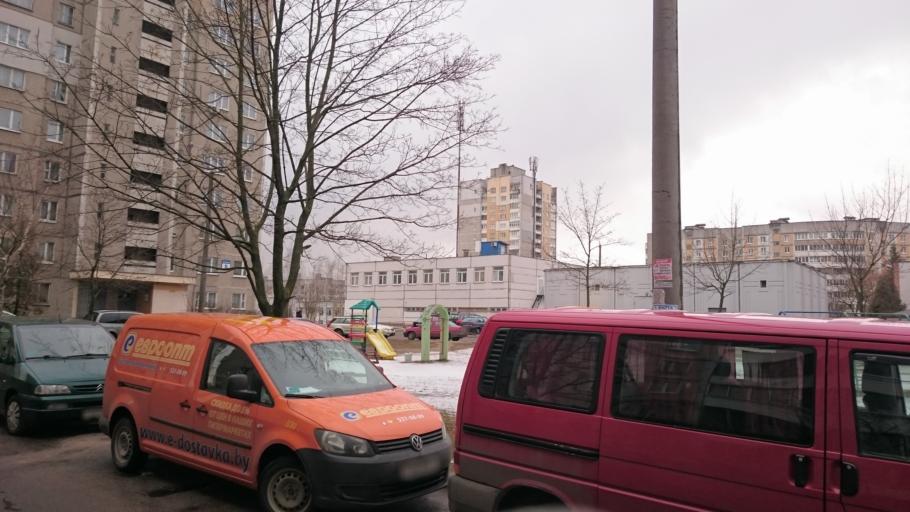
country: BY
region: Minsk
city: Borovlyany
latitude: 53.9367
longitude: 27.6862
